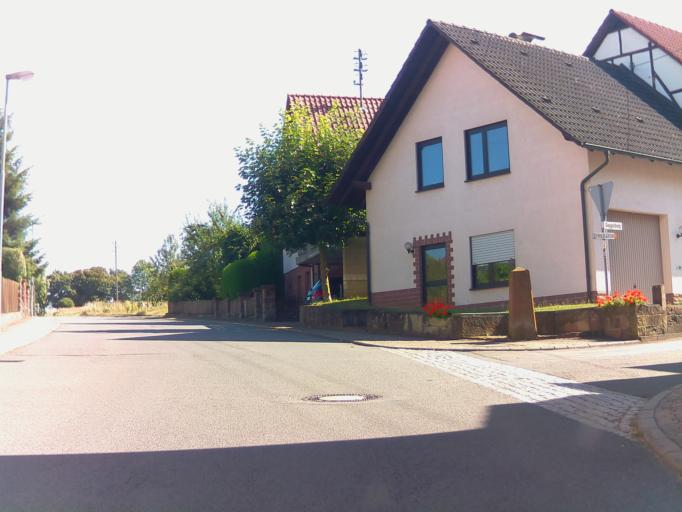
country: DE
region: Bavaria
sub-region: Regierungsbezirk Unterfranken
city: Neunkirchen
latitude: 49.7394
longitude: 9.3851
